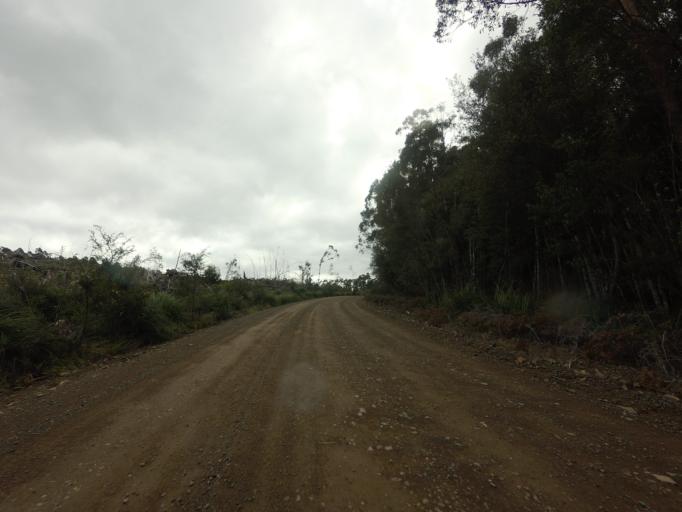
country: AU
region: Tasmania
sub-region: Huon Valley
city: Geeveston
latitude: -43.4890
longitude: 146.8886
